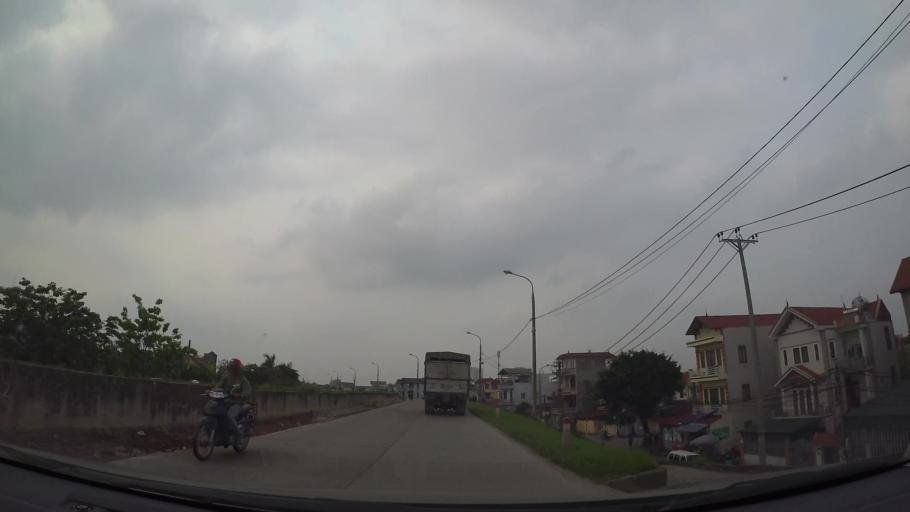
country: VN
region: Ha Noi
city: Trau Quy
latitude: 21.0066
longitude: 105.9077
